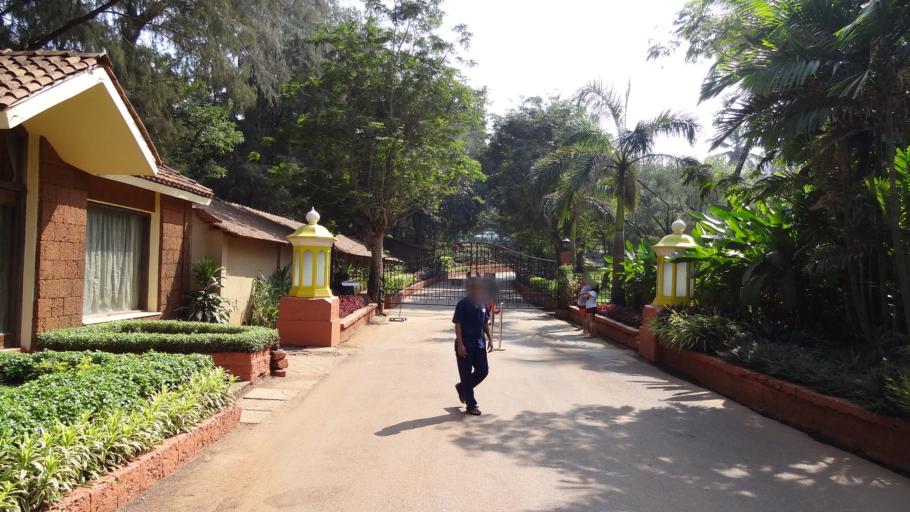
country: IN
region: Goa
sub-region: North Goa
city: Candolim
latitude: 15.4984
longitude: 73.7683
